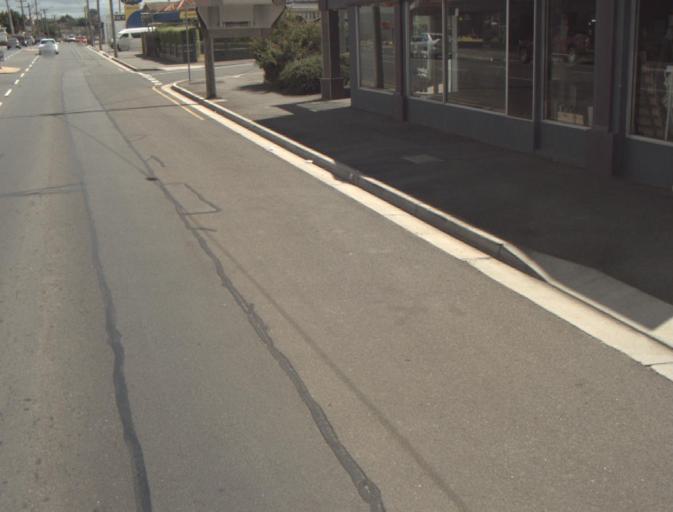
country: AU
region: Tasmania
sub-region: Launceston
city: Launceston
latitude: -41.4191
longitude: 147.1348
